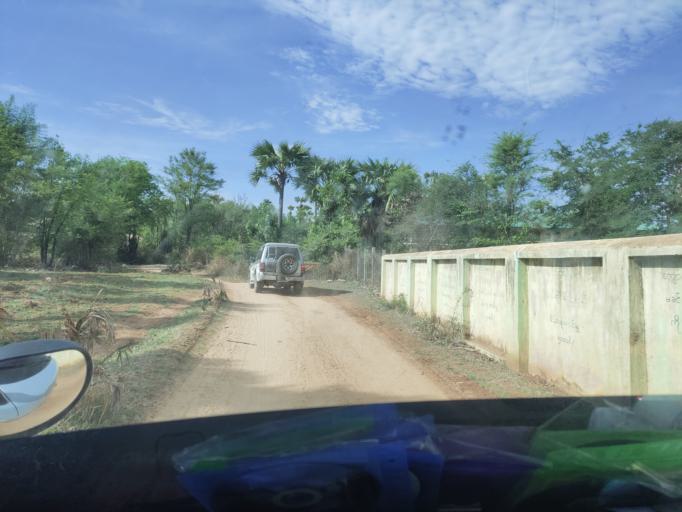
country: MM
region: Magway
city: Chauk
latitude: 20.9584
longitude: 94.9906
